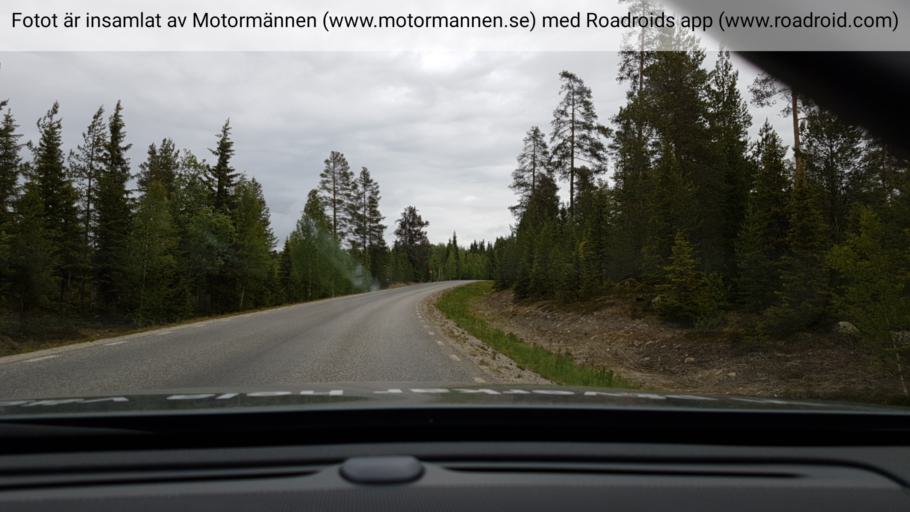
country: SE
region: Vaesterbotten
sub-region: Asele Kommun
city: Insjon
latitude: 64.3558
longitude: 17.9014
